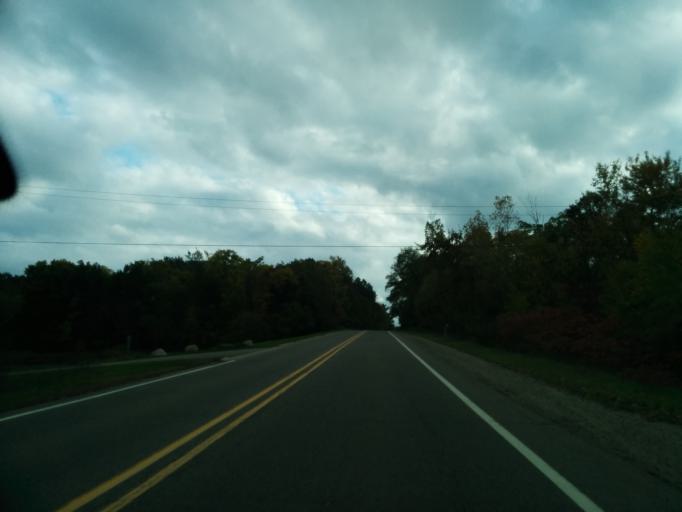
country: US
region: Michigan
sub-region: Oakland County
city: Waterford
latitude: 42.6555
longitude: -83.4934
